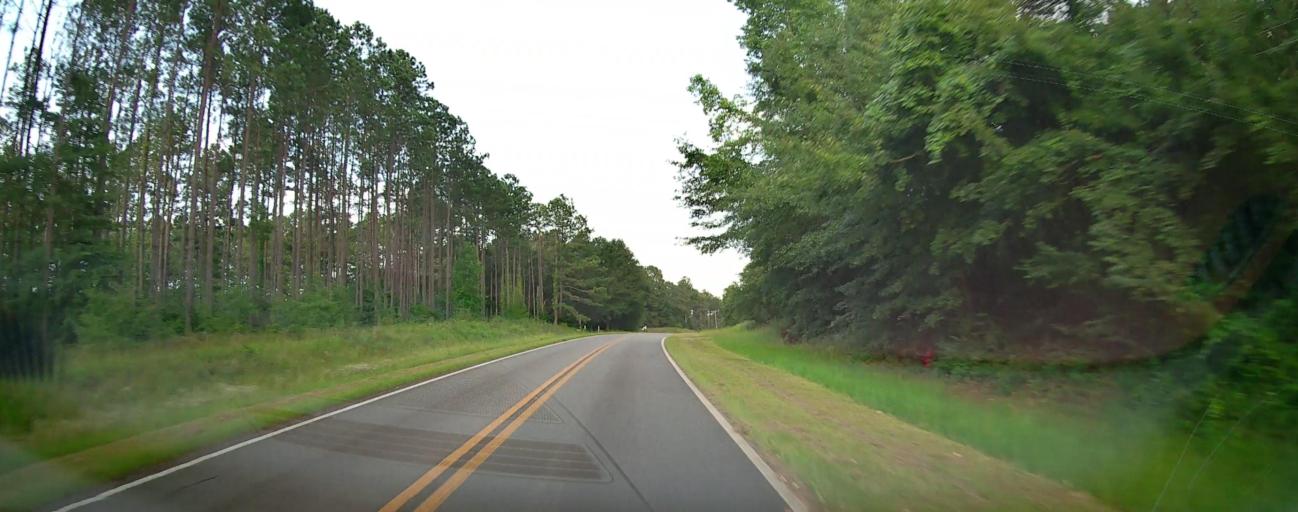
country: US
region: Georgia
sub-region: Crawford County
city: Roberta
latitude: 32.6713
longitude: -84.0751
